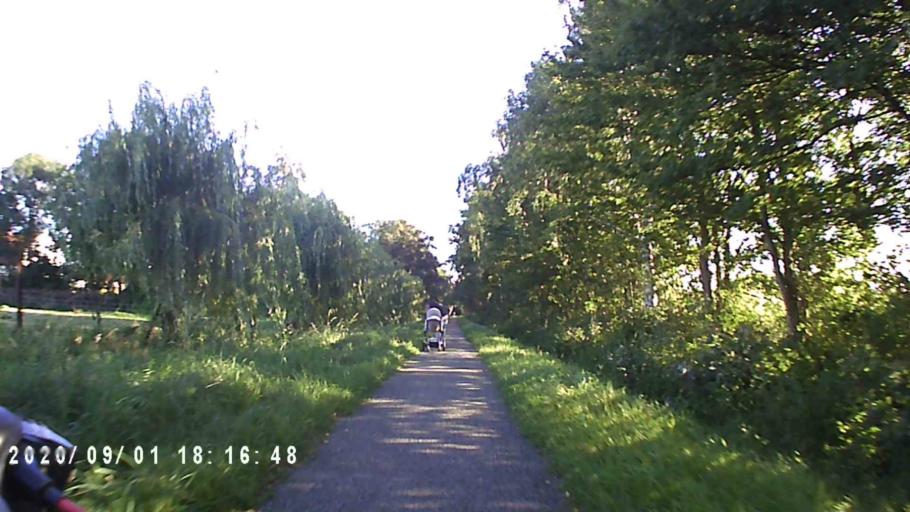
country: NL
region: Groningen
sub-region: Gemeente Hoogezand-Sappemeer
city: Sappemeer
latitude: 53.1751
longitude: 6.7865
